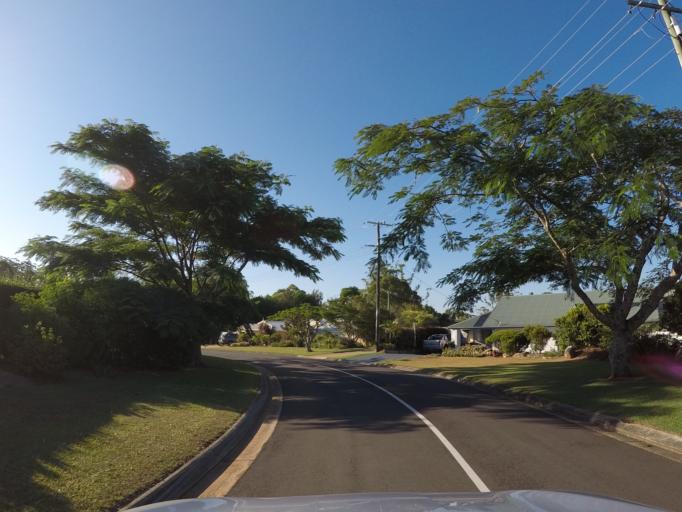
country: AU
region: Queensland
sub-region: Sunshine Coast
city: Nambour
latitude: -26.6184
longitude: 152.8655
